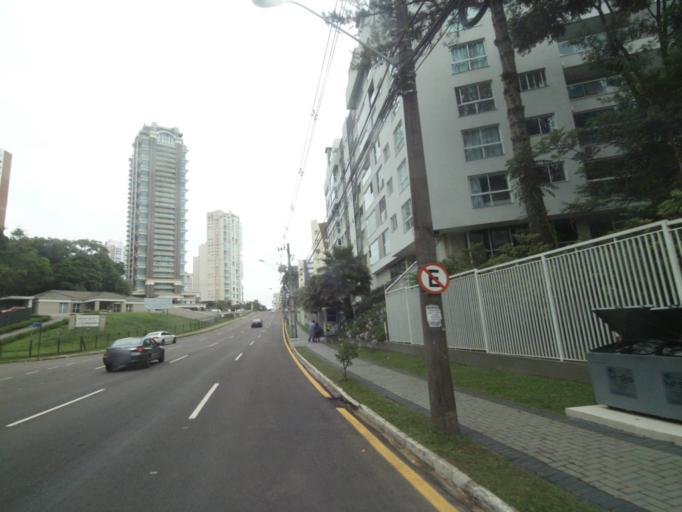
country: BR
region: Parana
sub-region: Curitiba
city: Curitiba
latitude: -25.4389
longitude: -49.3401
